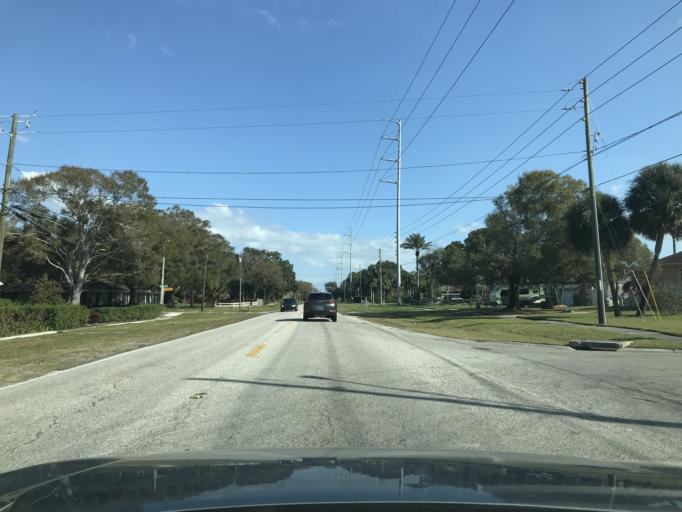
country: US
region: Florida
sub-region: Pinellas County
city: Largo
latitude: 27.9387
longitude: -82.7579
